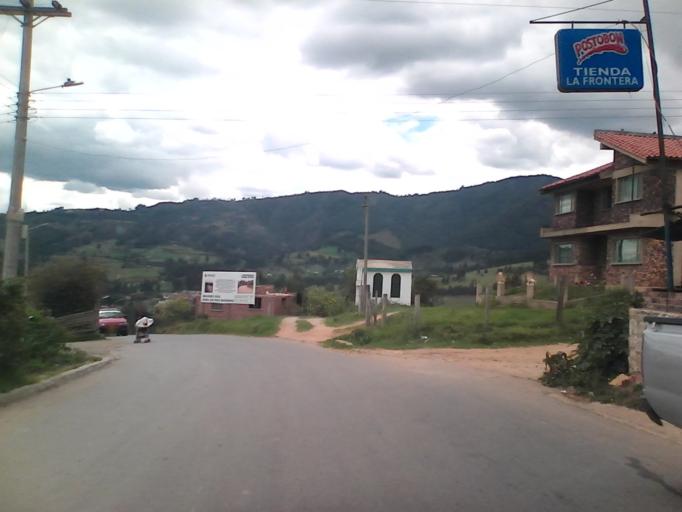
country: CO
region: Boyaca
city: Duitama
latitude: 5.8263
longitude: -73.0641
